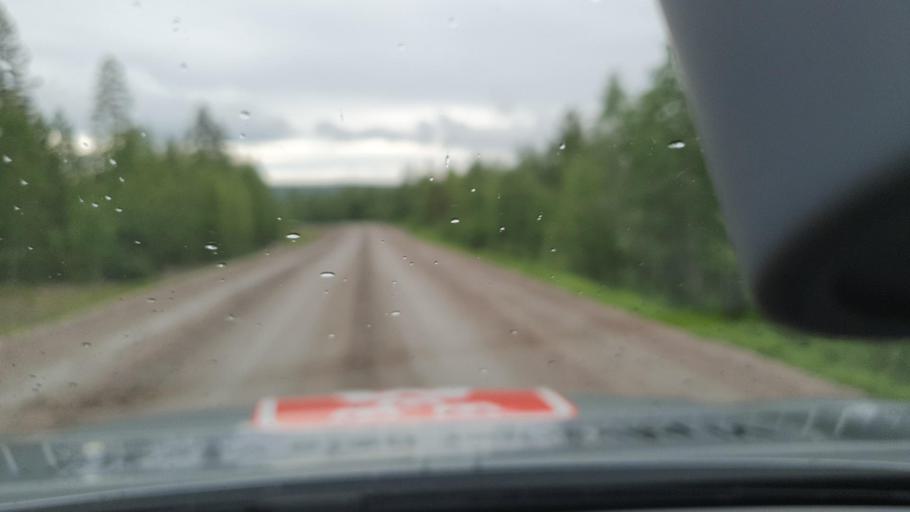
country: SE
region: Norrbotten
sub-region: Overtornea Kommun
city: OEvertornea
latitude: 66.4405
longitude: 23.4995
